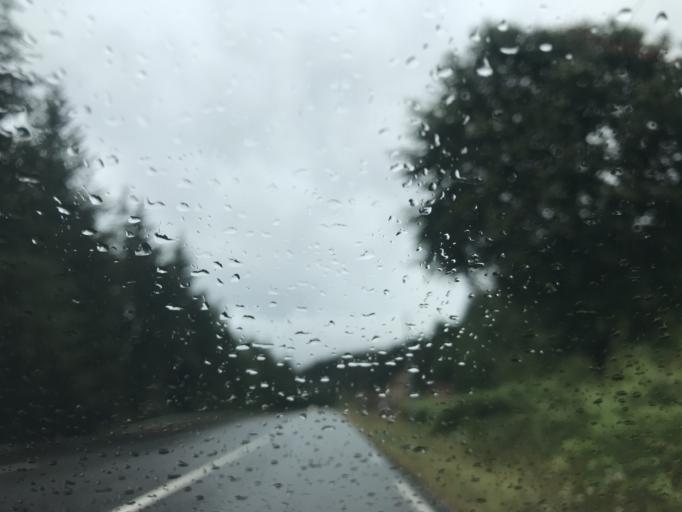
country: FR
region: Auvergne
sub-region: Departement du Puy-de-Dome
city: Job
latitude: 45.6043
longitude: 3.7204
